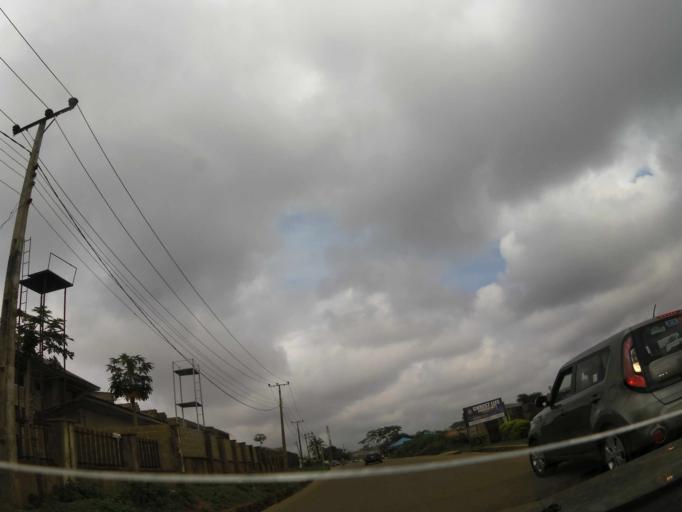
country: NG
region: Oyo
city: Ibadan
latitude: 7.4368
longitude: 3.9501
